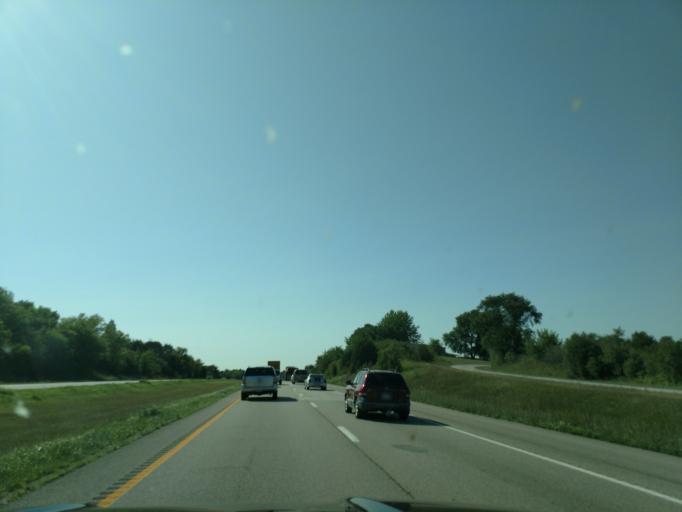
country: US
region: Missouri
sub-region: Andrew County
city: Country Club Village
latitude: 39.8774
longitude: -94.8421
